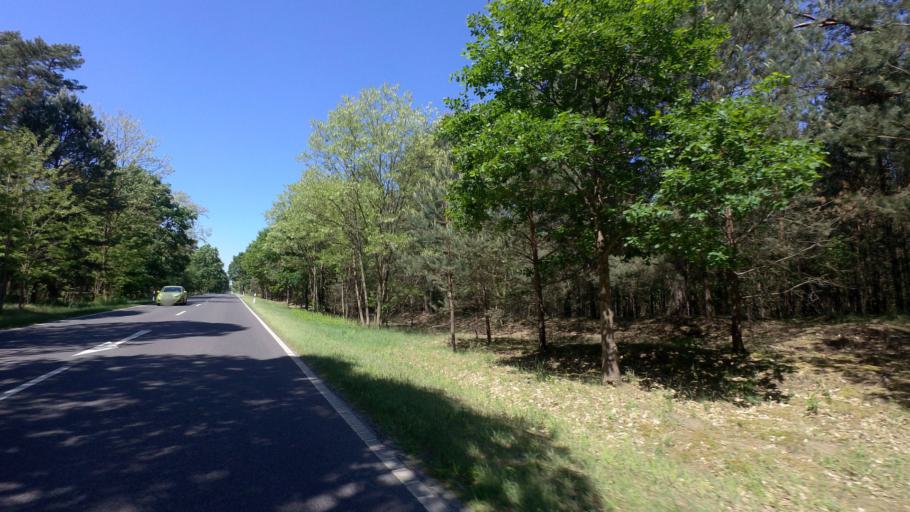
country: DE
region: Brandenburg
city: Lieberose
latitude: 51.9569
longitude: 14.3279
